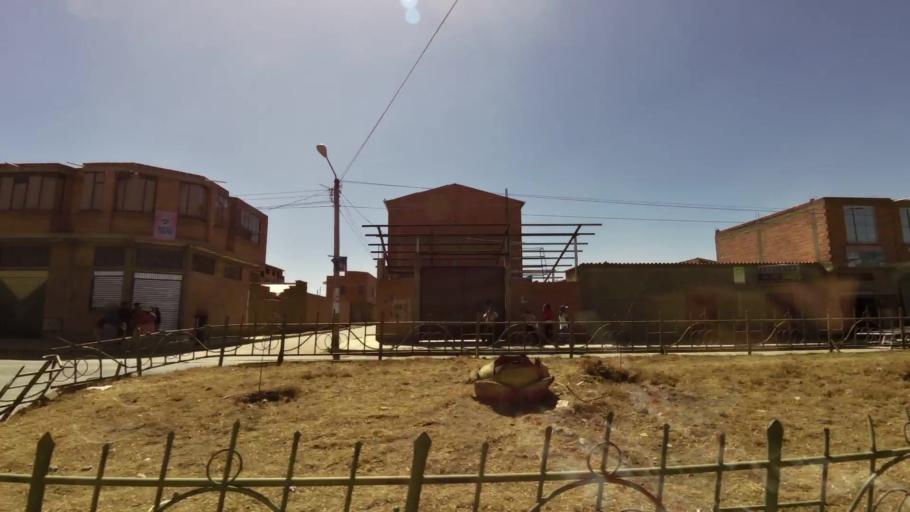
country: BO
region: La Paz
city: La Paz
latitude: -16.5035
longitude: -68.2224
